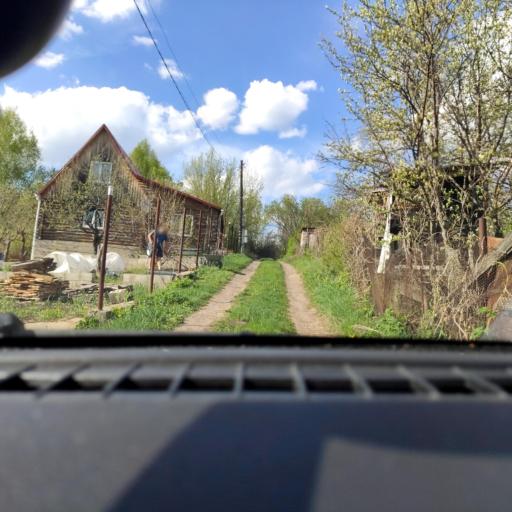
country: RU
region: Samara
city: Zhigulevsk
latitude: 53.3696
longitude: 49.5084
